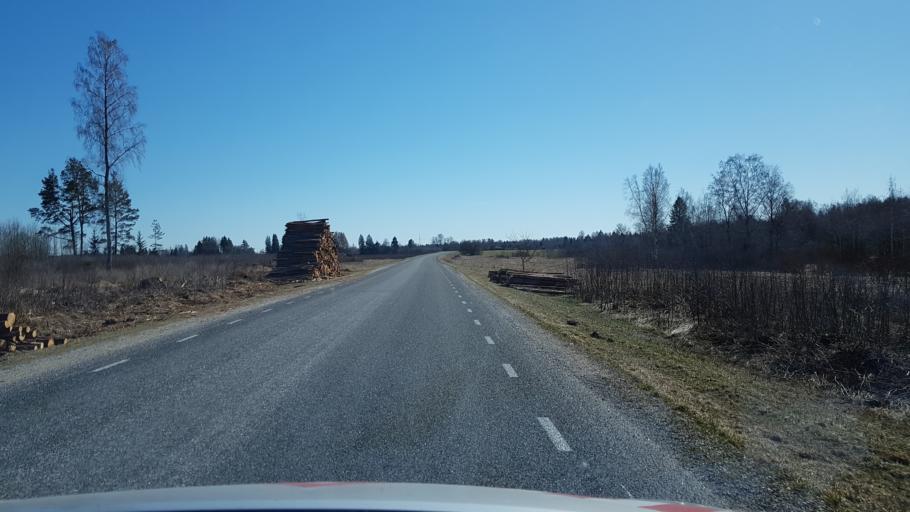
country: EE
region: Laeaene-Virumaa
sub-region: Someru vald
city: Someru
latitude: 59.3857
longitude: 26.4412
